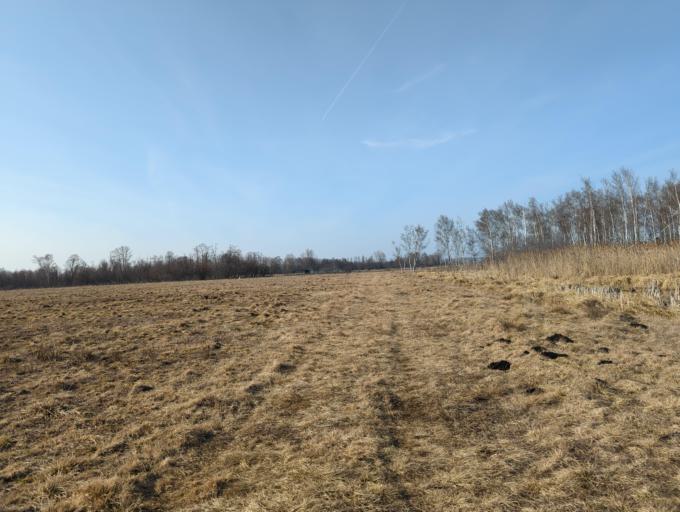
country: DE
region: Bavaria
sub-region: Swabia
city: Leipheim
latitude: 48.4857
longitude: 10.2145
